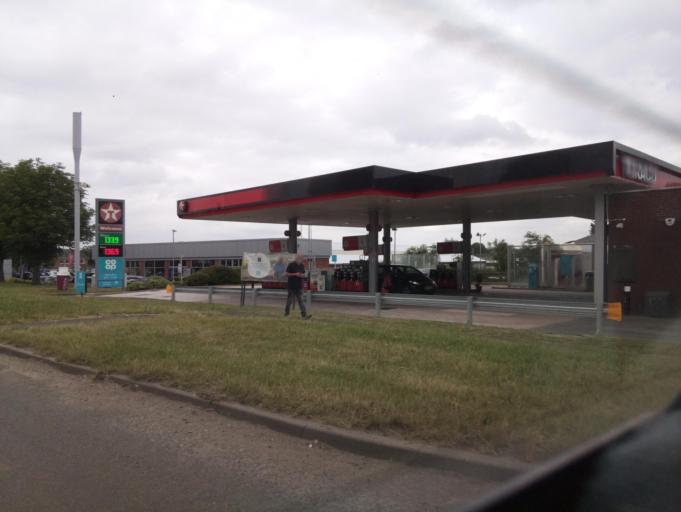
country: GB
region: England
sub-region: Staffordshire
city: Penkridge
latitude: 52.7175
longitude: -2.1187
